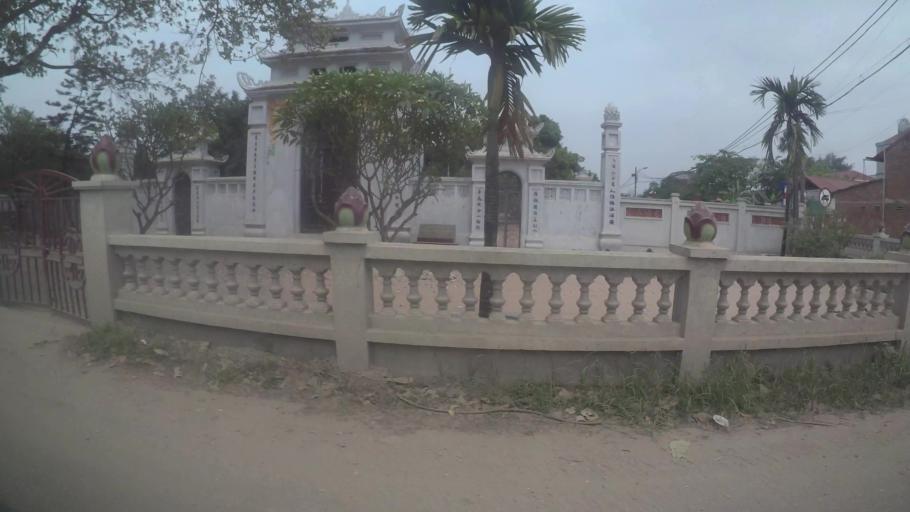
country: VN
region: Ha Noi
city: Cau Dien
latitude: 21.0366
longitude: 105.7381
